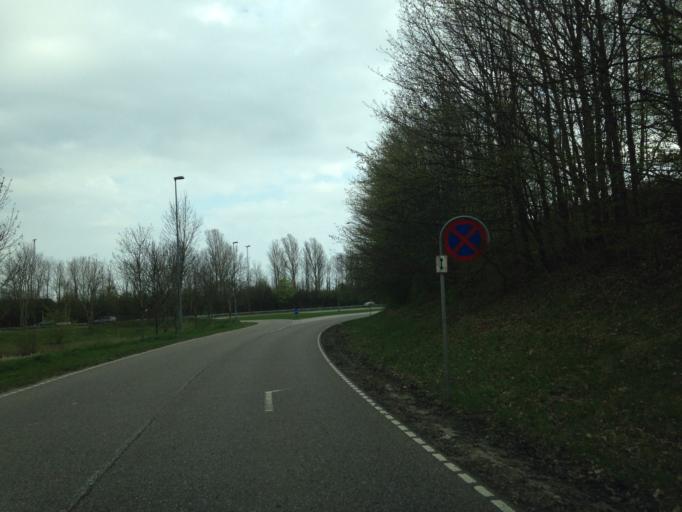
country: DK
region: Capital Region
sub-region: Hoje-Taastrup Kommune
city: Taastrup
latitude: 55.6412
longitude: 12.2791
